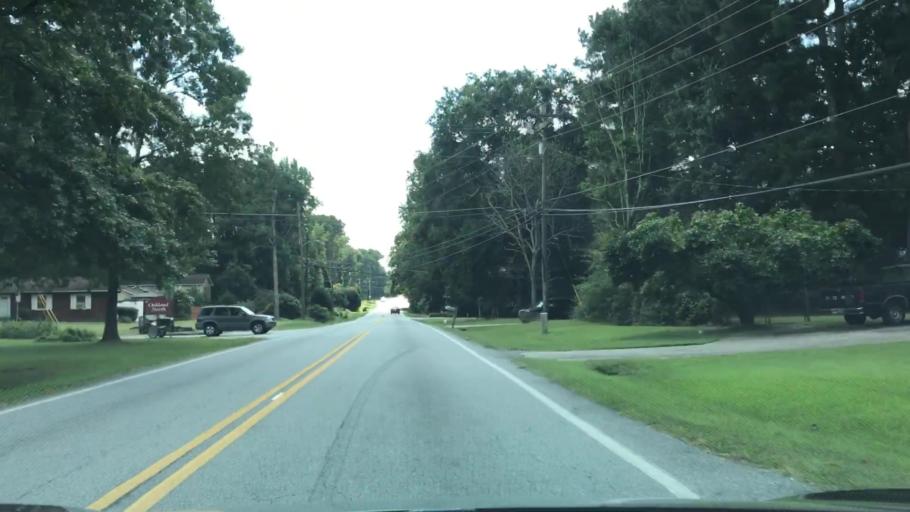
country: US
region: Georgia
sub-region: Gwinnett County
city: Lawrenceville
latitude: 33.9442
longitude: -84.0619
